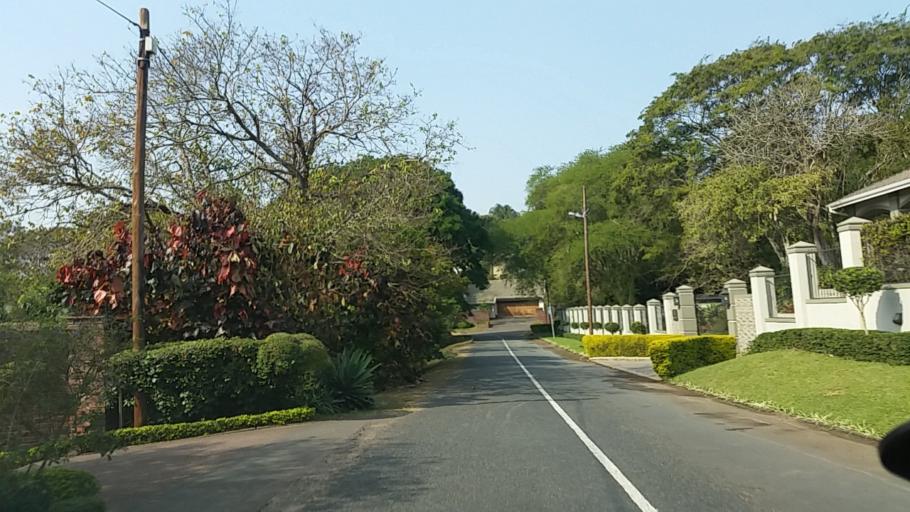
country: ZA
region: KwaZulu-Natal
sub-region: eThekwini Metropolitan Municipality
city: Berea
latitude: -29.8334
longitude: 30.9294
